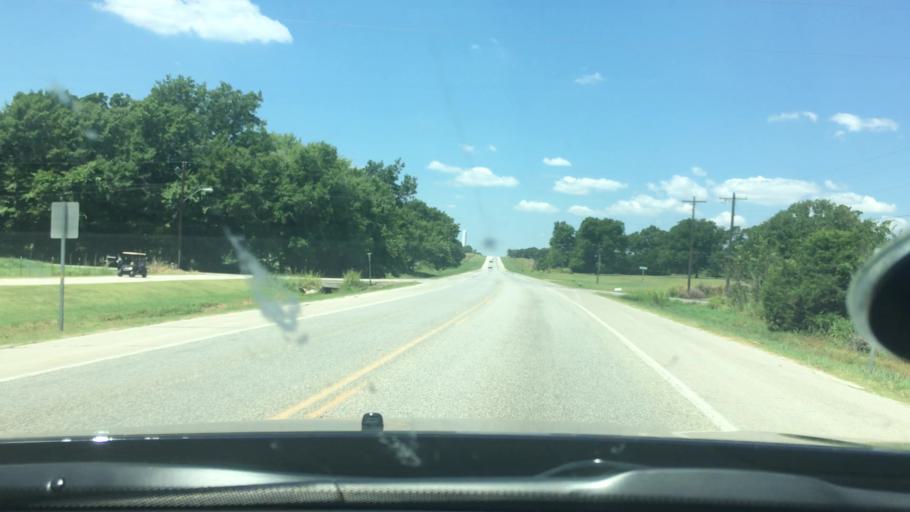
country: US
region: Oklahoma
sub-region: Carter County
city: Dickson
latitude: 34.1872
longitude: -96.8972
